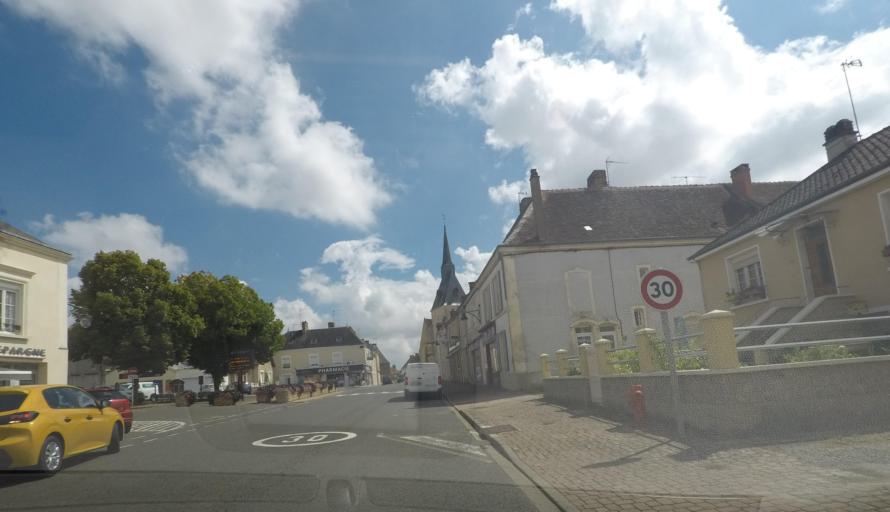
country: FR
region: Pays de la Loire
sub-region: Departement de la Sarthe
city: Saint-Cosme-en-Vairais
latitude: 48.2733
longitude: 0.4592
